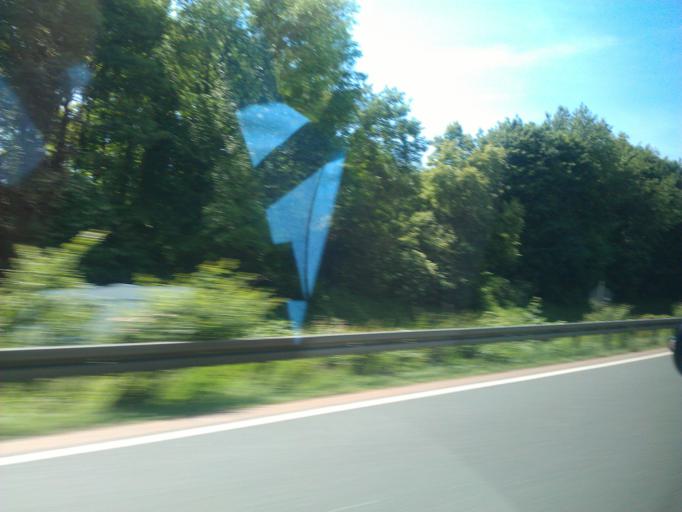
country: DE
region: North Rhine-Westphalia
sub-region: Regierungsbezirk Koln
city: Bad Honnef
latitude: 50.6772
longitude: 7.2884
